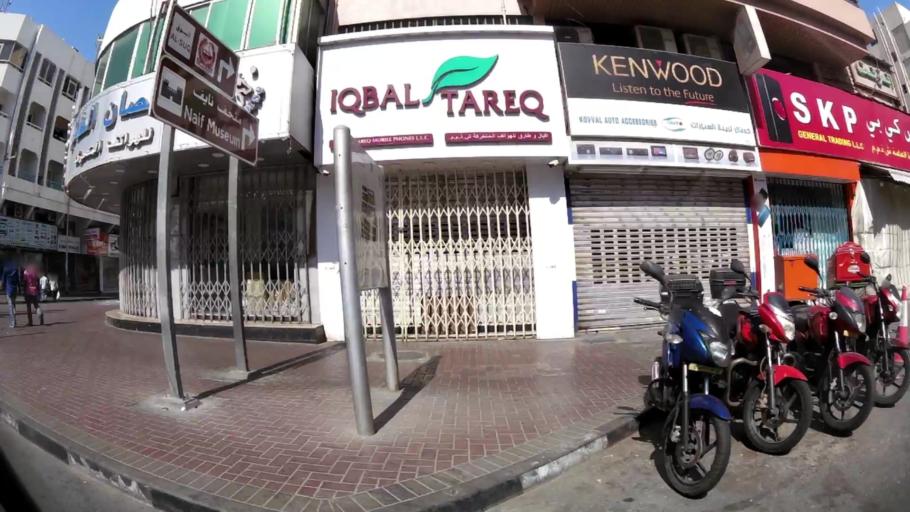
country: AE
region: Ash Shariqah
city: Sharjah
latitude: 25.2746
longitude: 55.3060
